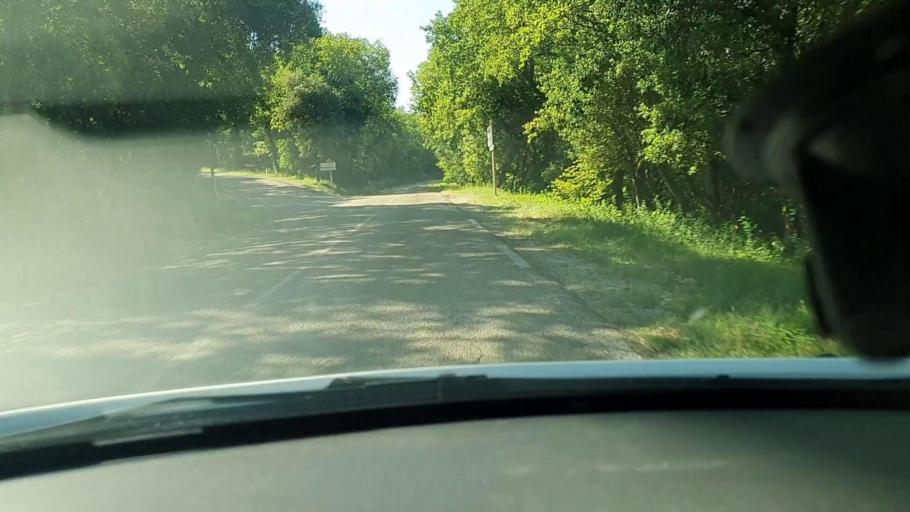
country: FR
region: Languedoc-Roussillon
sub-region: Departement du Gard
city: Saint-Paulet-de-Caisson
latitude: 44.2396
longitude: 4.5707
